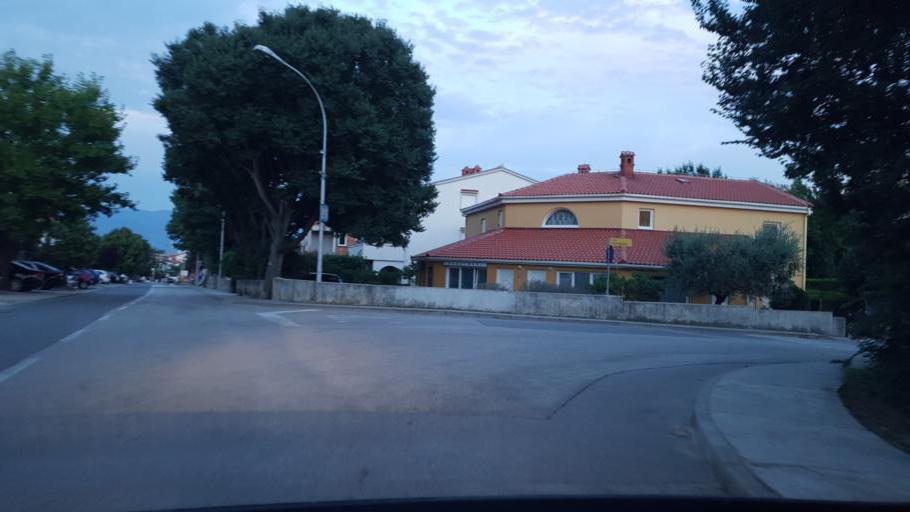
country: HR
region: Primorsko-Goranska
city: Punat
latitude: 44.9718
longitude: 14.7453
